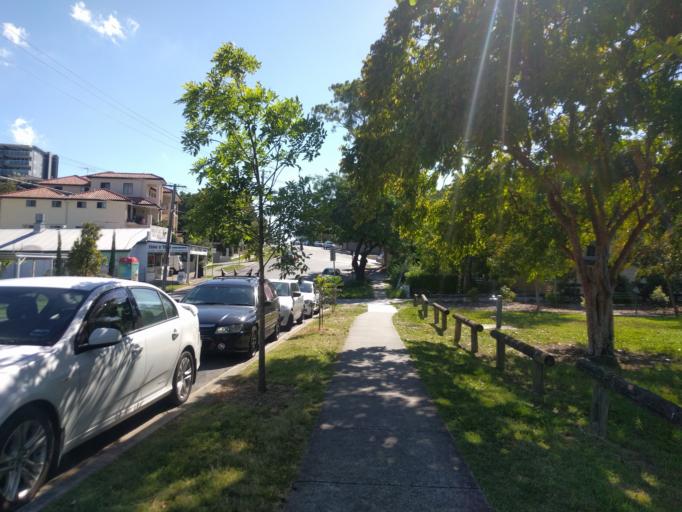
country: AU
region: Queensland
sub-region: Brisbane
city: Milton
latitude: -27.4750
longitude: 152.9989
